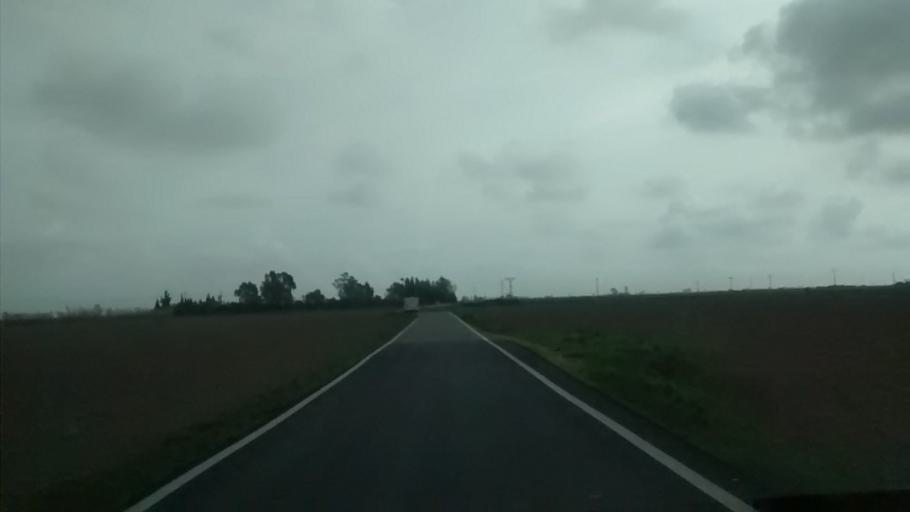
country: ES
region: Catalonia
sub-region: Provincia de Tarragona
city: Sant Carles de la Rapita
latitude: 40.6521
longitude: 0.6232
